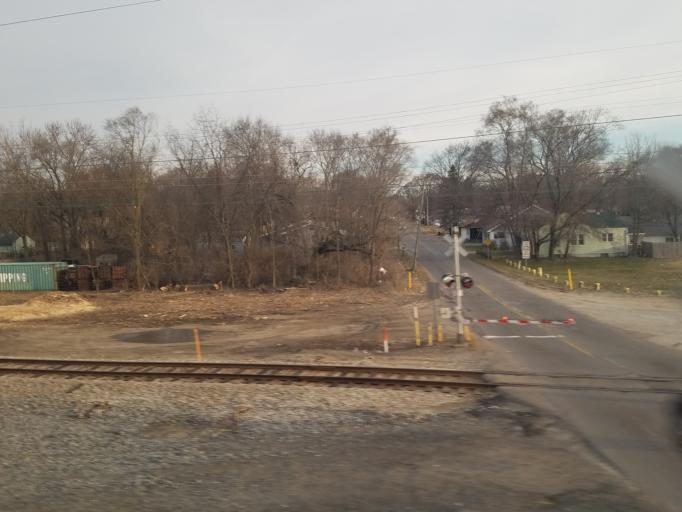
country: US
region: Indiana
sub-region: Saint Joseph County
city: South Bend
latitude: 41.6833
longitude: -86.3100
